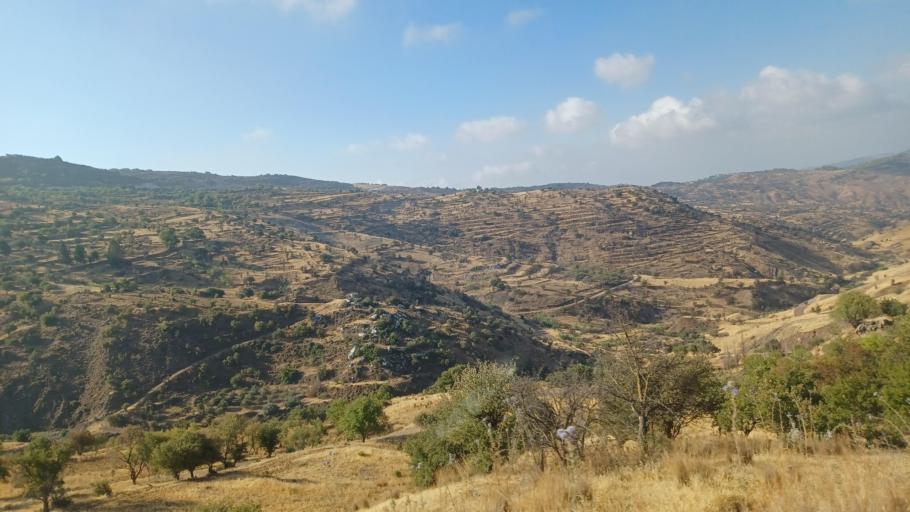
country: CY
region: Pafos
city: Mesogi
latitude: 34.8697
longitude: 32.6088
